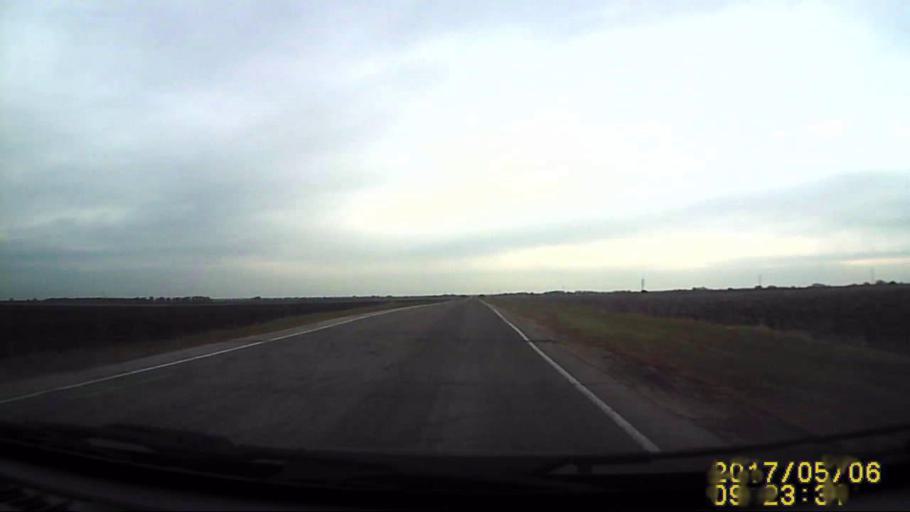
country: RU
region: Ulyanovsk
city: Cherdakly
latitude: 54.3762
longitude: 48.7919
